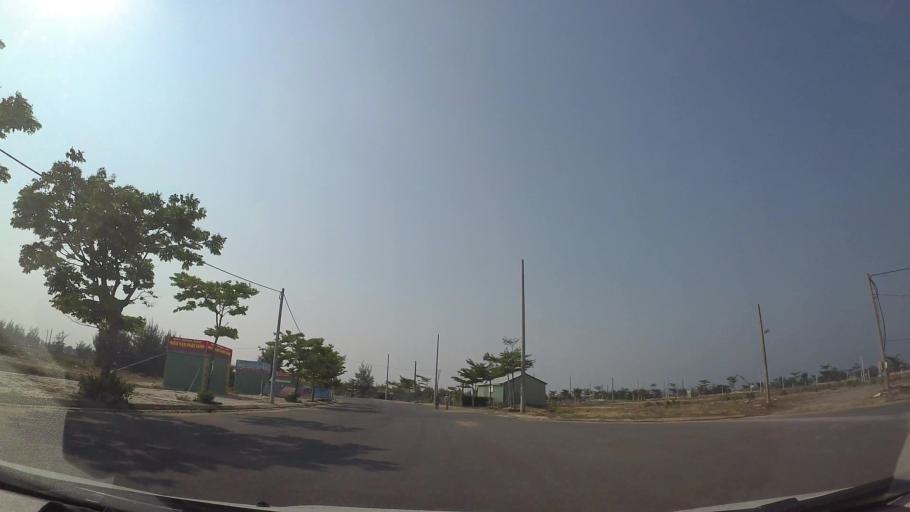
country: VN
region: Da Nang
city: Ngu Hanh Son
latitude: 15.9542
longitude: 108.2739
